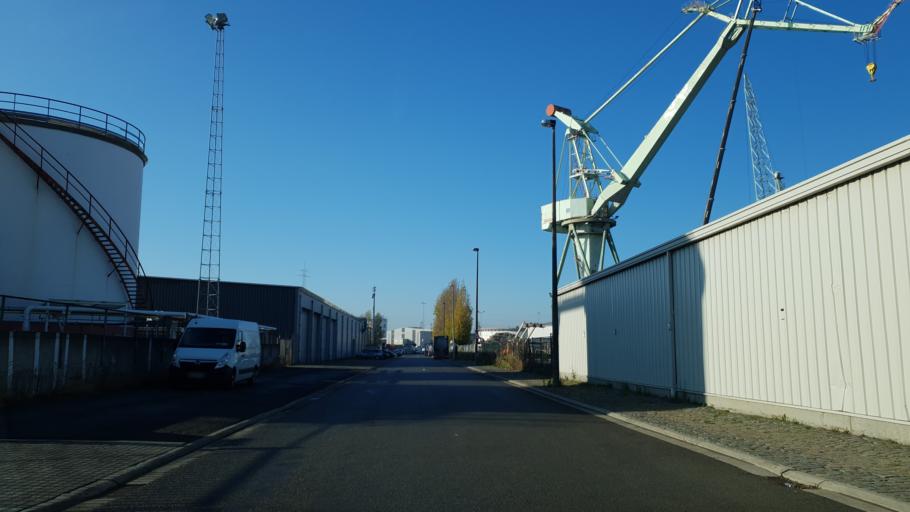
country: BE
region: Flanders
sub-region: Provincie Antwerpen
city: Zwijndrecht
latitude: 51.2507
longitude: 4.3570
